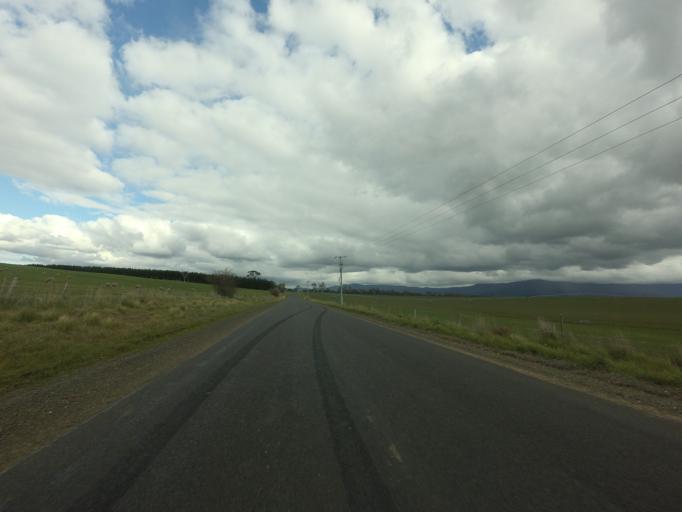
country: AU
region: Tasmania
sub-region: Northern Midlands
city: Longford
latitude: -41.7562
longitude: 147.0825
